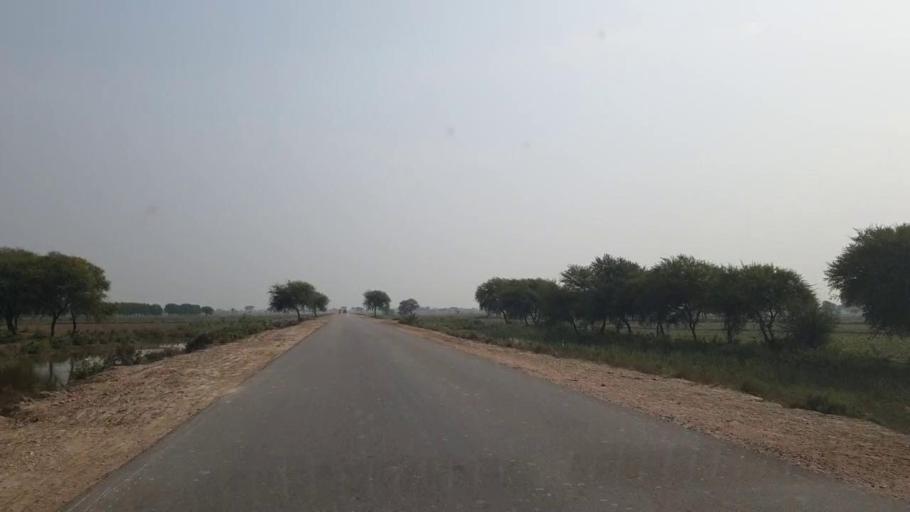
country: PK
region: Sindh
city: Matli
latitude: 25.0608
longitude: 68.6675
